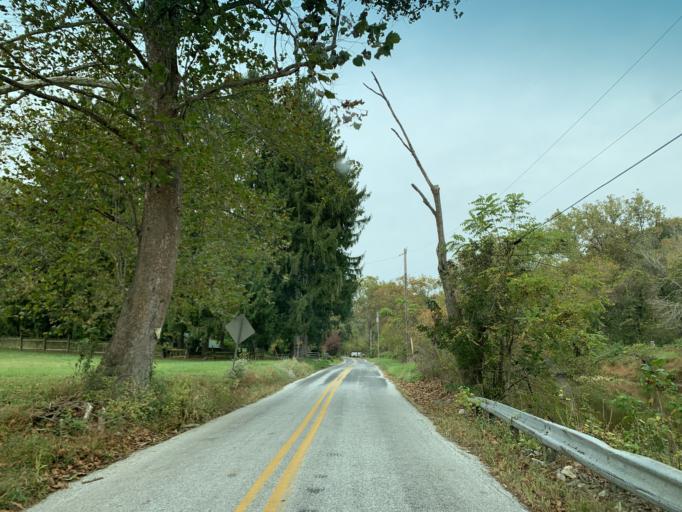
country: US
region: Pennsylvania
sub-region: York County
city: Susquehanna Trails
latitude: 39.7862
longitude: -76.4076
